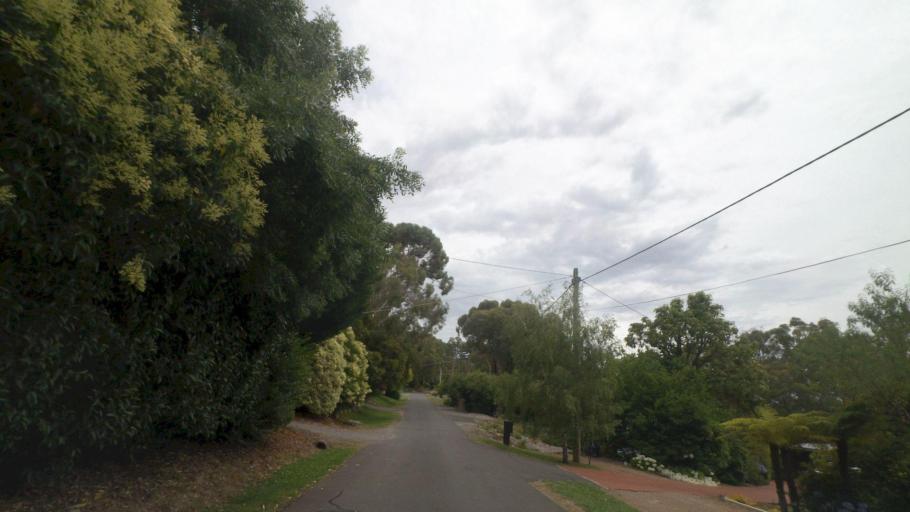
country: AU
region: Victoria
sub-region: Knox
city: The Basin
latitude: -37.8513
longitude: 145.3304
